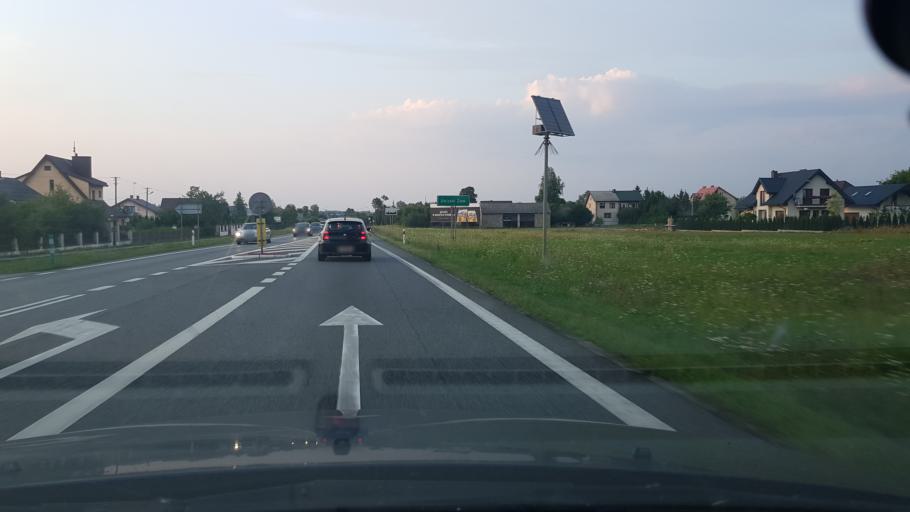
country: PL
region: Masovian Voivodeship
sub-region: Powiat mlawski
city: Mlawa
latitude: 53.1602
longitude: 20.4112
